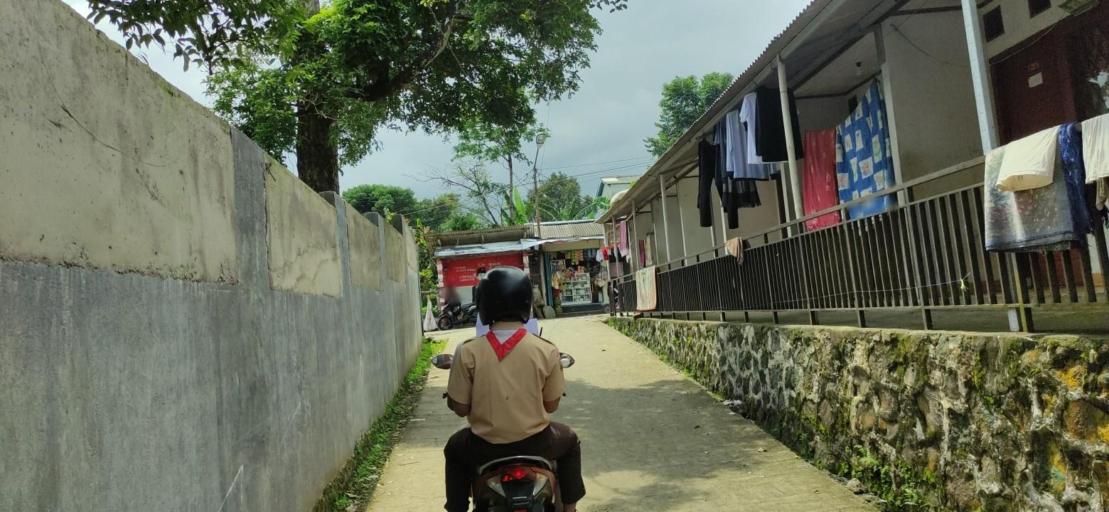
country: ID
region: West Java
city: Caringin
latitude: -6.6443
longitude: 106.8887
